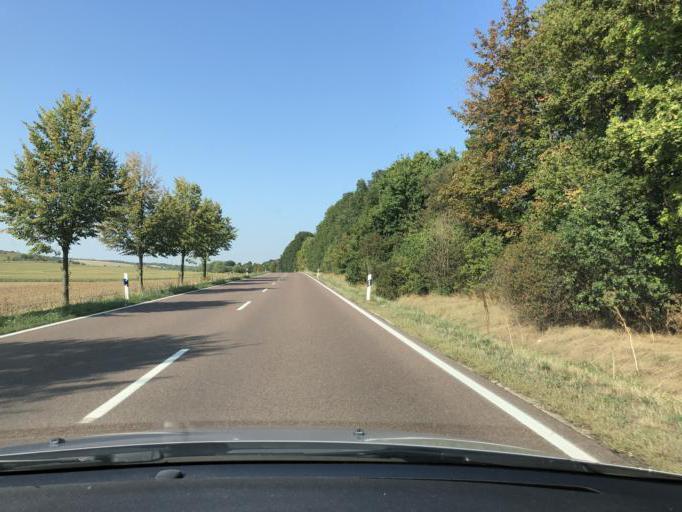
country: DE
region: Saxony-Anhalt
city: Freyburg
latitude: 51.2341
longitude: 11.8136
